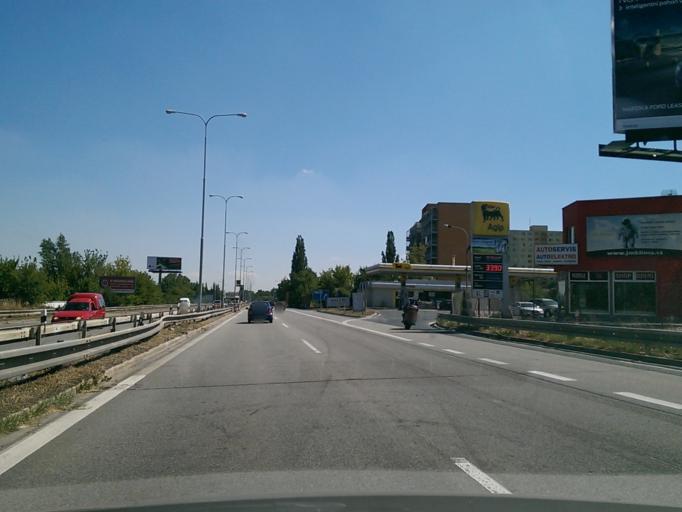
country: CZ
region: South Moravian
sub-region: Mesto Brno
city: Mokra Hora
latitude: 49.2353
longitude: 16.5910
